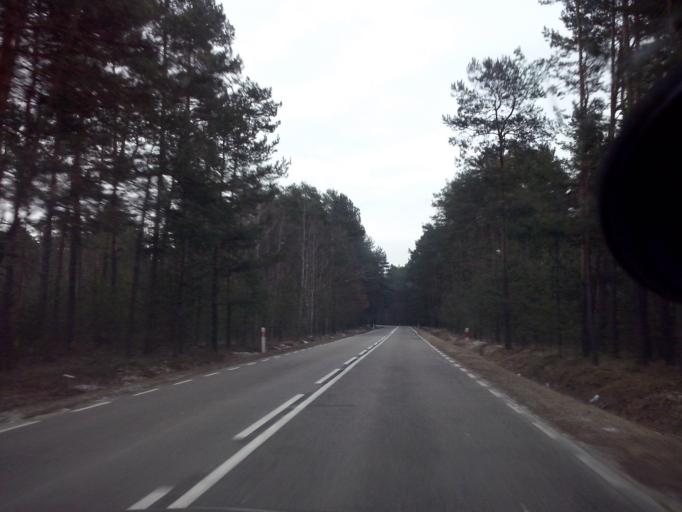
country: PL
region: Lublin Voivodeship
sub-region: Powiat bilgorajski
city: Biszcza
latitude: 50.5034
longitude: 22.5925
